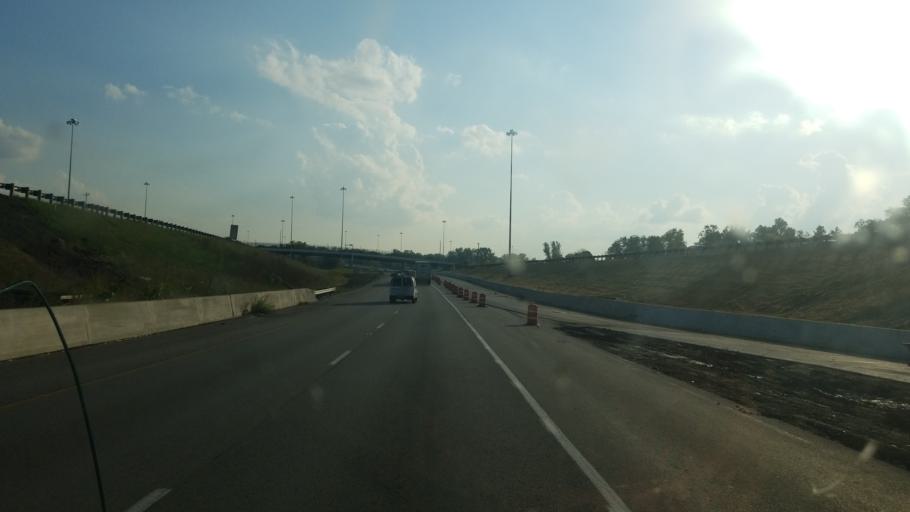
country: US
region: Ohio
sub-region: Lucas County
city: Toledo
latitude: 41.6817
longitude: -83.5713
